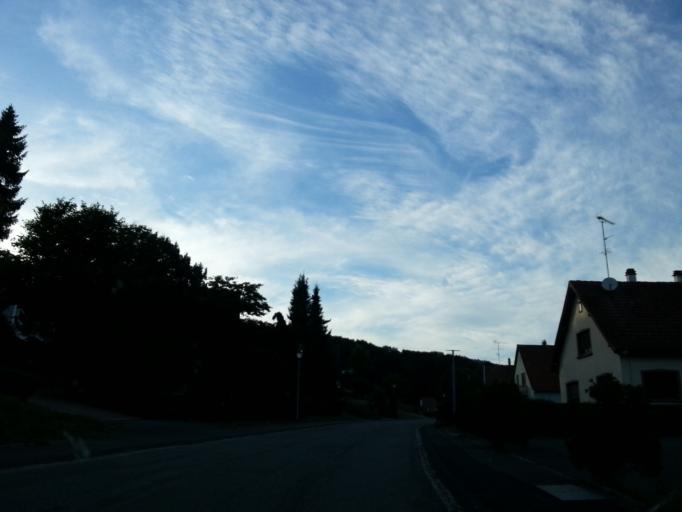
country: FR
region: Alsace
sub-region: Departement du Bas-Rhin
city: Soultz-sous-Forets
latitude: 48.9788
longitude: 7.8766
